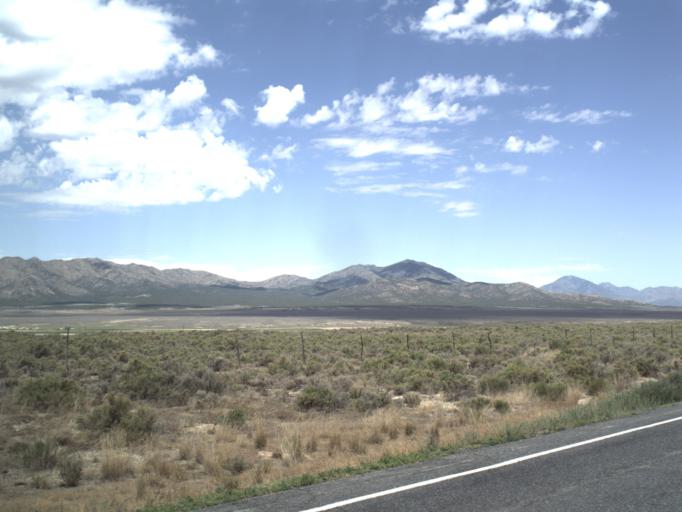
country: US
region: Utah
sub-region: Tooele County
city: Tooele
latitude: 40.1195
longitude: -112.4308
